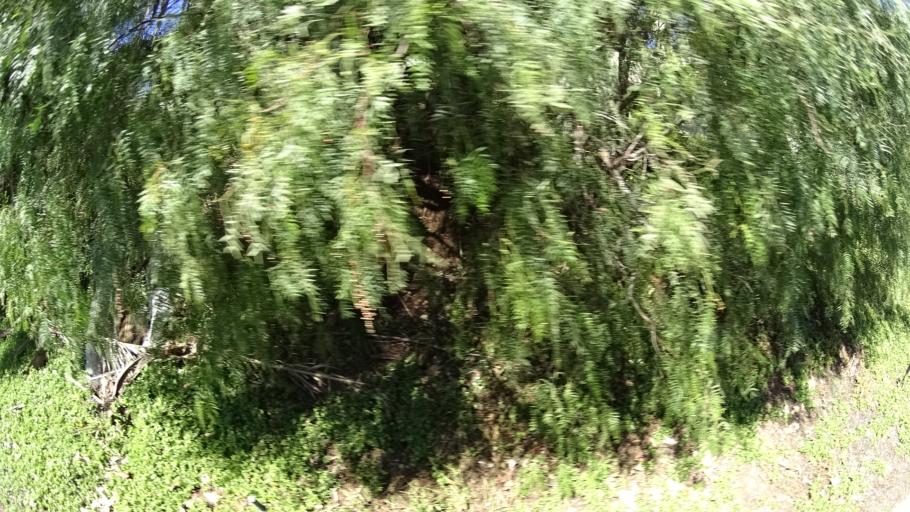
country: US
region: California
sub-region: Orange County
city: Villa Park
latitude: 33.8490
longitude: -117.8041
